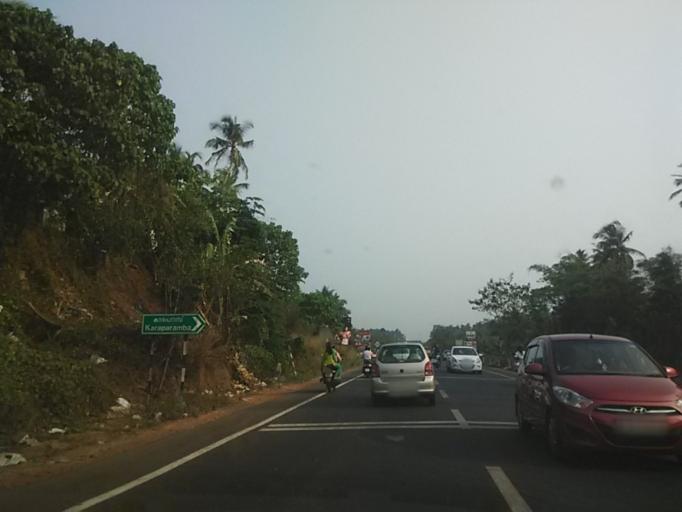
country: IN
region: Kerala
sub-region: Kozhikode
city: Kozhikode
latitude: 11.2944
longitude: 75.7976
